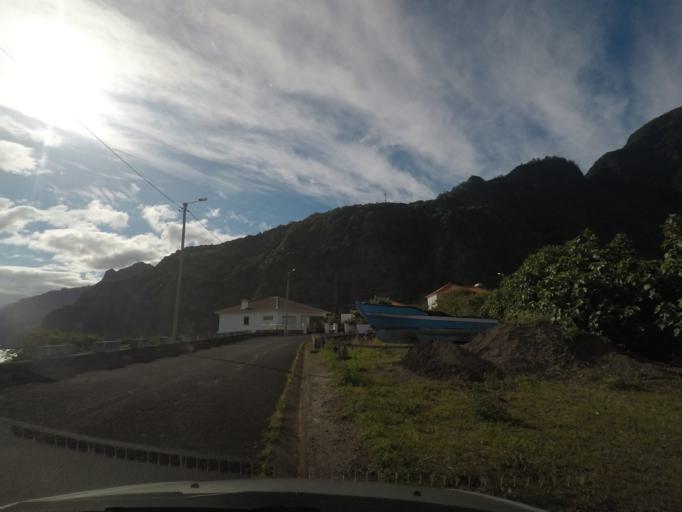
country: PT
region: Madeira
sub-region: Sao Vicente
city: Sao Vicente
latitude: 32.8283
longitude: -16.9887
